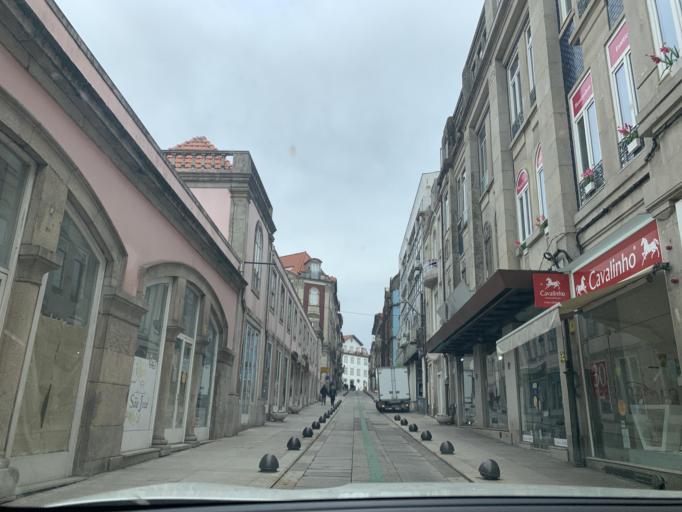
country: PT
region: Viseu
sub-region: Viseu
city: Viseu
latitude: 40.6576
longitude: -7.9123
